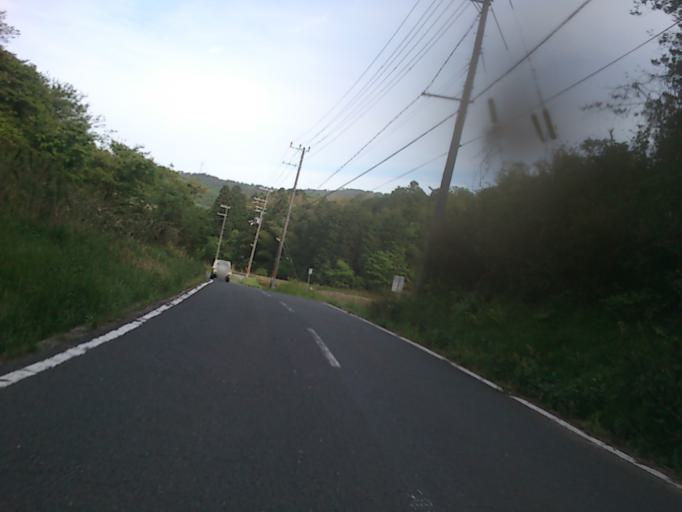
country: JP
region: Kyoto
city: Miyazu
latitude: 35.5729
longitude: 135.1125
